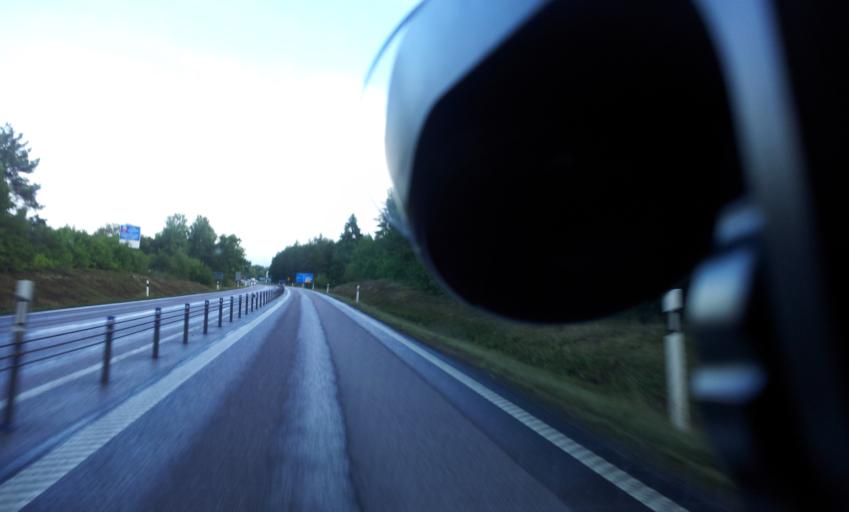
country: SE
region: Kalmar
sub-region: Monsteras Kommun
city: Moensteras
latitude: 57.0183
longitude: 16.4279
